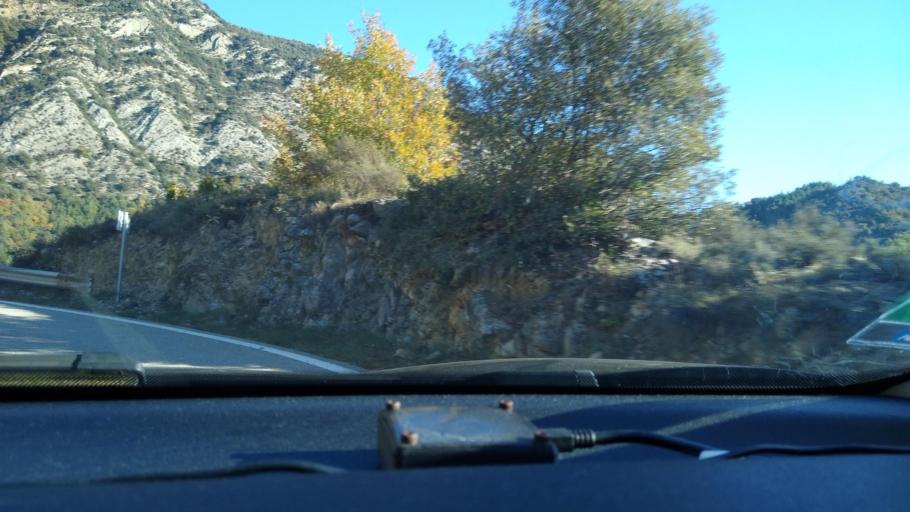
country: ES
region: Catalonia
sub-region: Provincia de Barcelona
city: Guardiola de Bergueda
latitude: 42.2202
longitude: 1.8551
